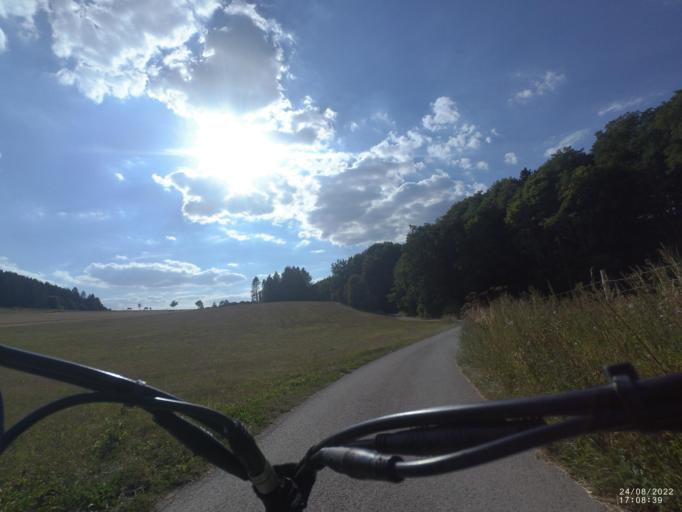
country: DE
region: Rheinland-Pfalz
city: Dohm-Lammersdorf
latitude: 50.2635
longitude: 6.6713
